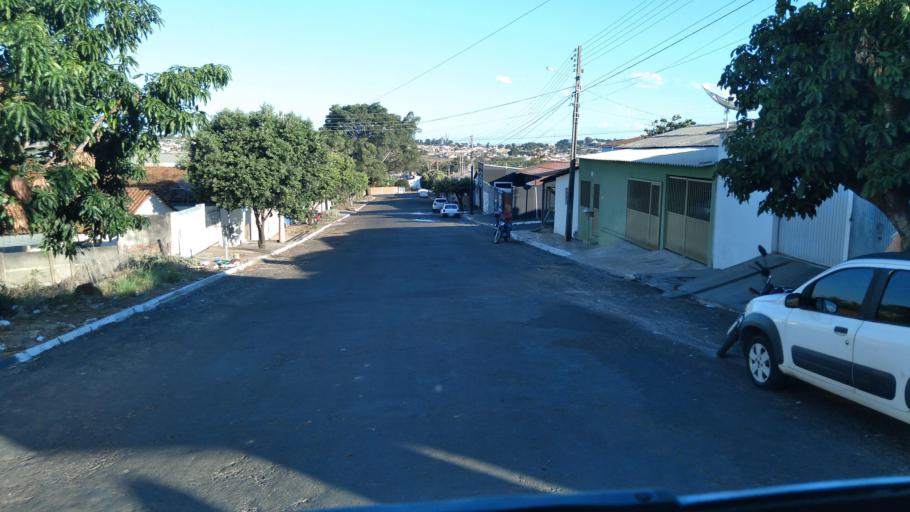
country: BR
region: Goias
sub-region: Mineiros
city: Mineiros
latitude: -17.5599
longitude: -52.5459
